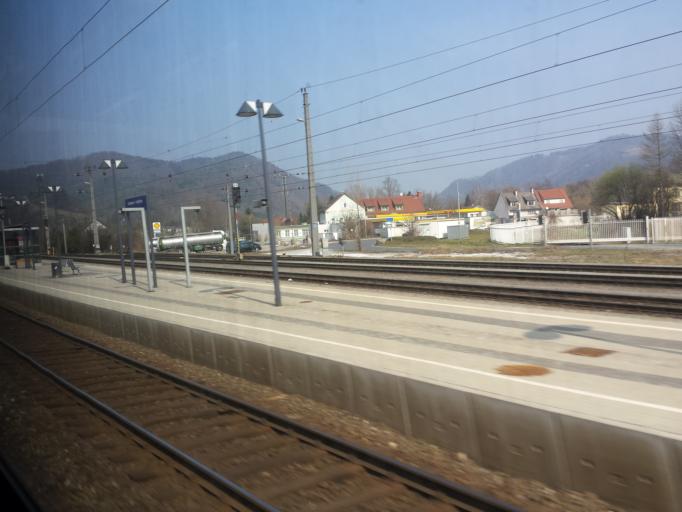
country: AT
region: Styria
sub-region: Politischer Bezirk Graz-Umgebung
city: Gratwein
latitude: 47.1286
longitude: 15.3238
